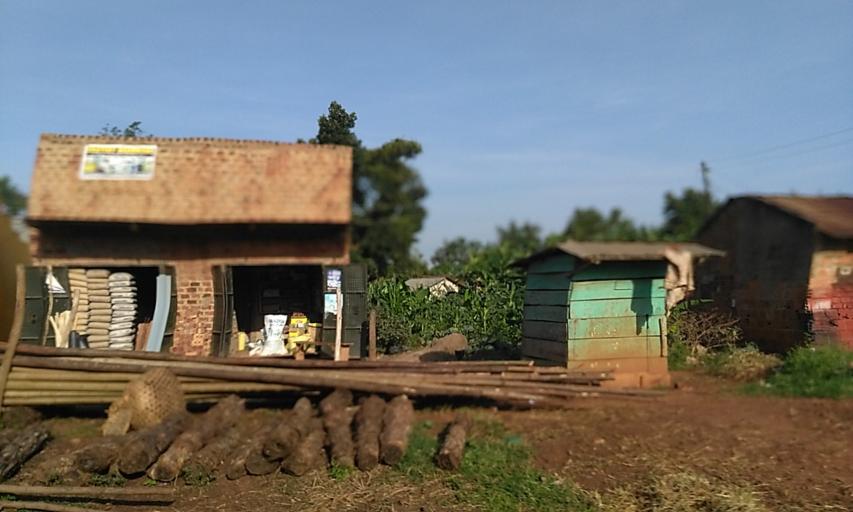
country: UG
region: Central Region
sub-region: Wakiso District
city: Bweyogerere
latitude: 0.4689
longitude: 32.6588
